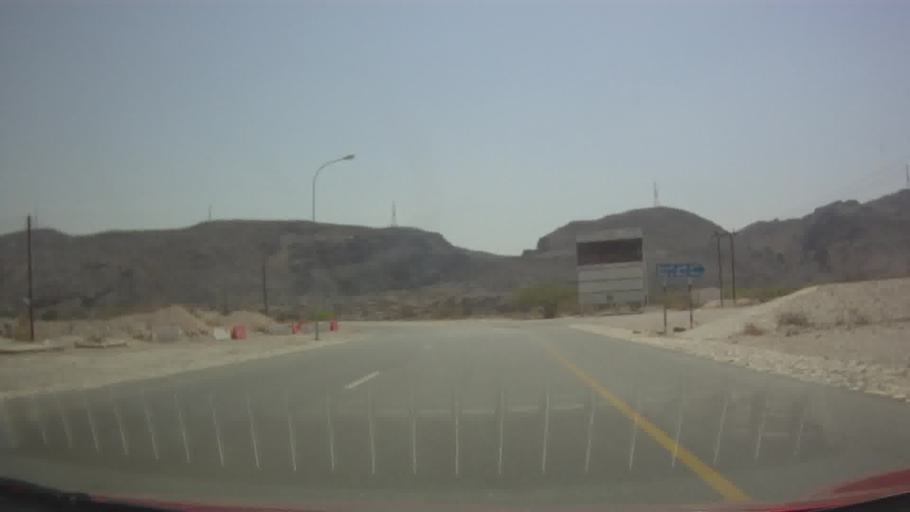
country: OM
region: Muhafazat Masqat
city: Muscat
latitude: 23.5122
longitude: 58.6345
